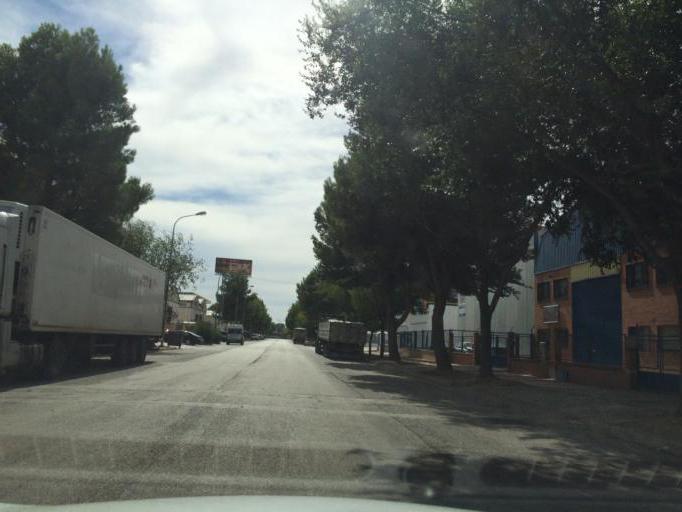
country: ES
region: Castille-La Mancha
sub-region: Provincia de Albacete
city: Albacete
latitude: 39.0230
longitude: -1.8812
